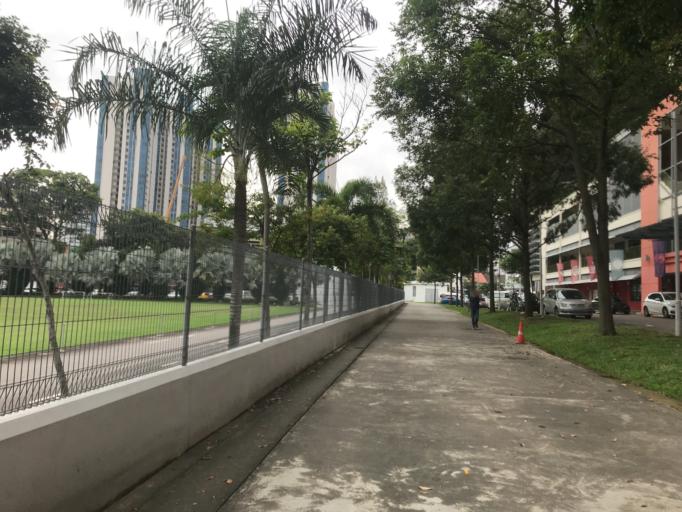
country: SG
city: Singapore
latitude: 1.3093
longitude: 103.8601
